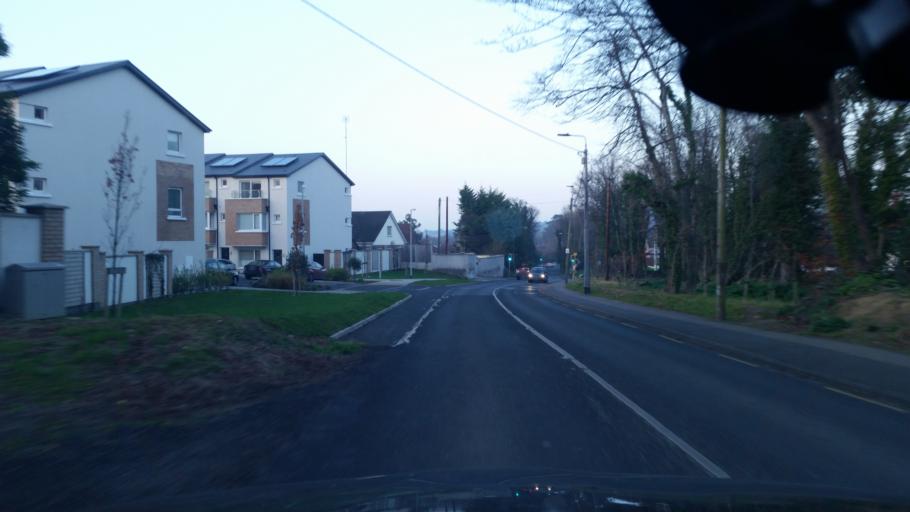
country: IE
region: Leinster
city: Shankill
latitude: 53.2356
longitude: -6.1229
